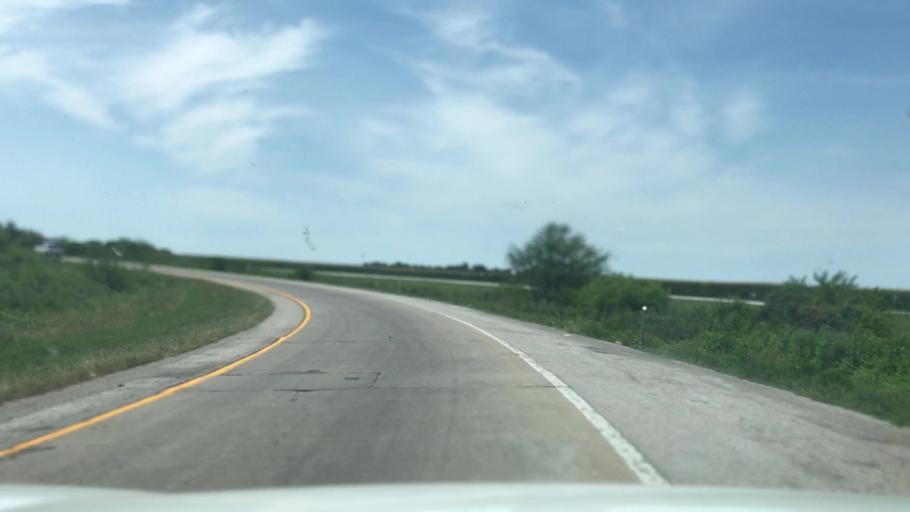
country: US
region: Illinois
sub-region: Clinton County
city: New Baden
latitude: 38.5363
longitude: -89.7264
